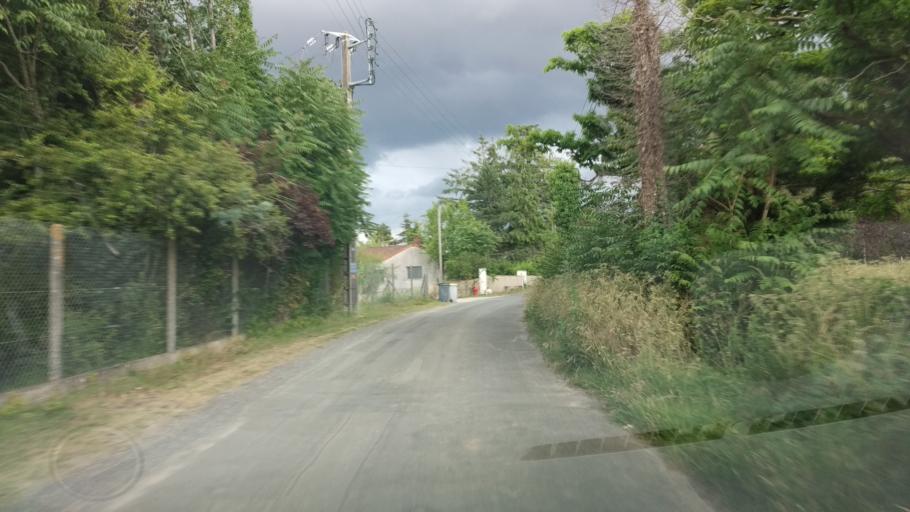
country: FR
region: Poitou-Charentes
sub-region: Departement de la Vienne
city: Migne-Auxances
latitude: 46.6251
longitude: 0.3458
